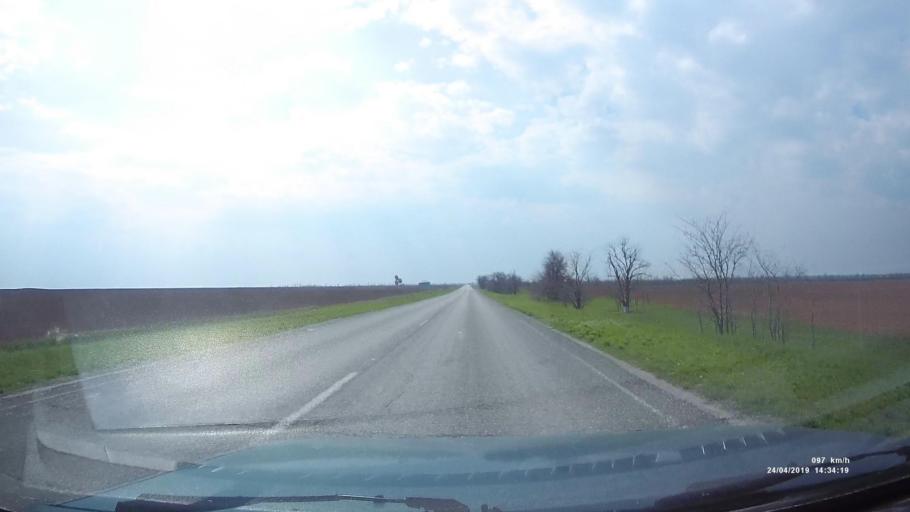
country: RU
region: Kalmykiya
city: Arshan'
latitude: 46.3737
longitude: 43.9341
